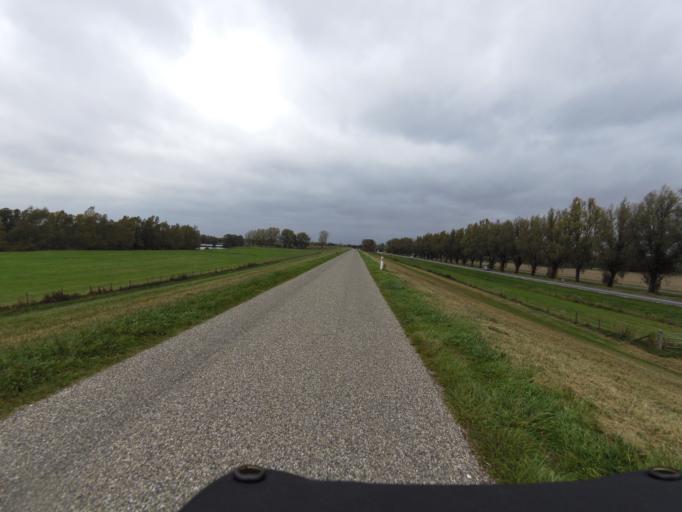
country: NL
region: Gelderland
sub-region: Gemeente Zevenaar
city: Zevenaar
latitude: 51.8771
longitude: 6.1000
